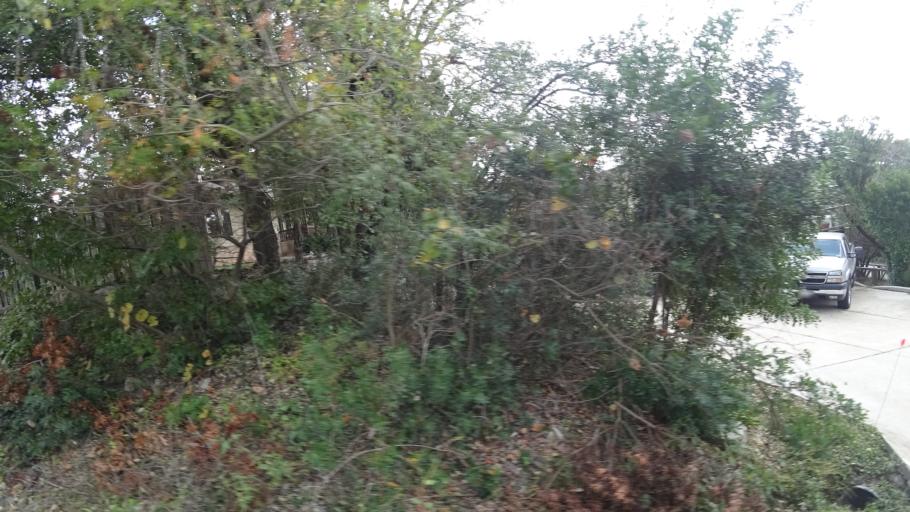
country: US
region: Texas
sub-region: Travis County
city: Hudson Bend
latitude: 30.3841
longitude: -97.9295
